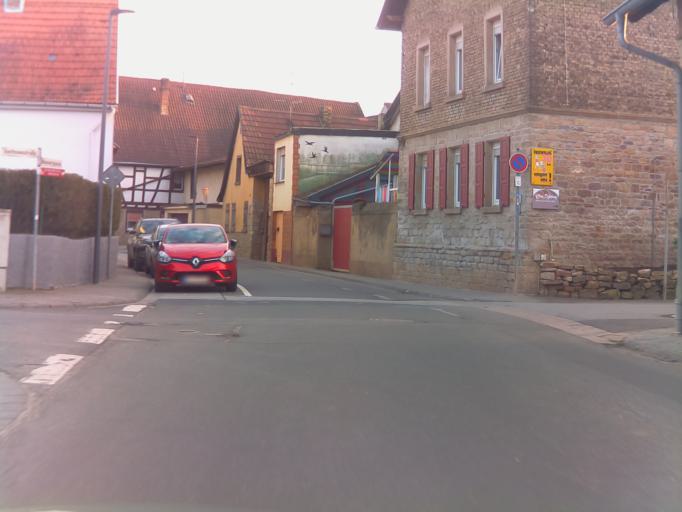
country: DE
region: Rheinland-Pfalz
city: Wallertheim
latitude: 49.8378
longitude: 8.0504
